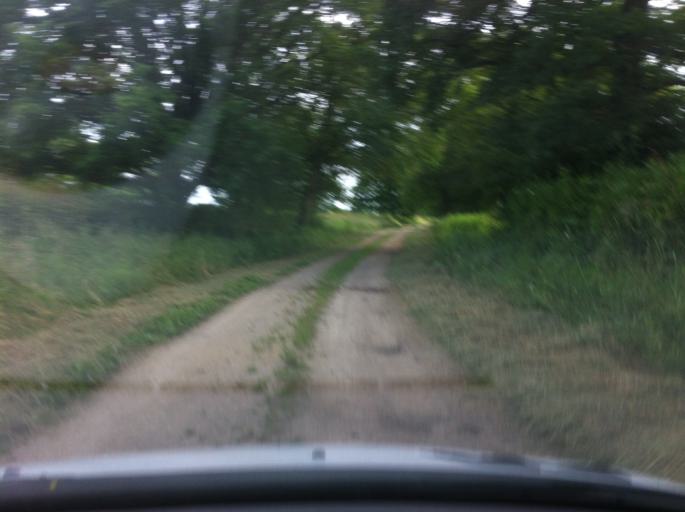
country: FR
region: Auvergne
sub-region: Departement de l'Allier
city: Chantelle
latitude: 46.3216
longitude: 3.1073
